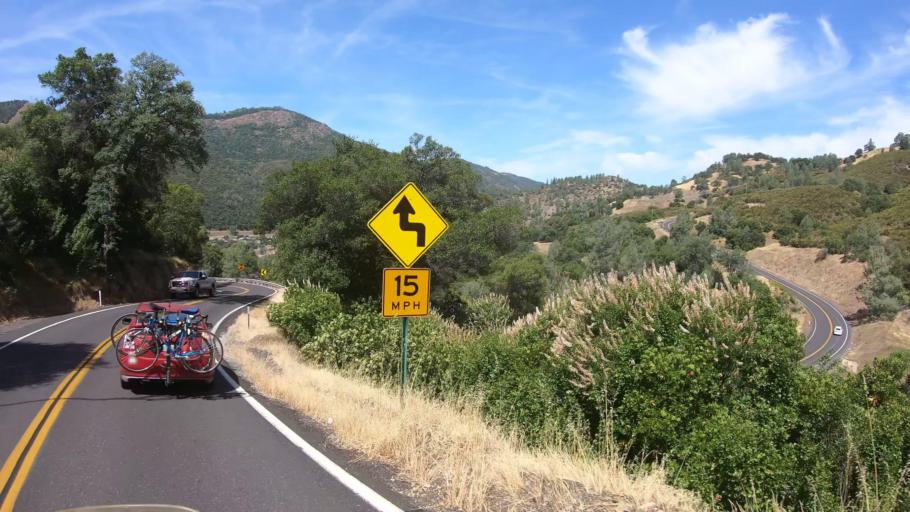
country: US
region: California
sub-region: Tuolumne County
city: Tuolumne City
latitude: 37.8158
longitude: -120.2969
